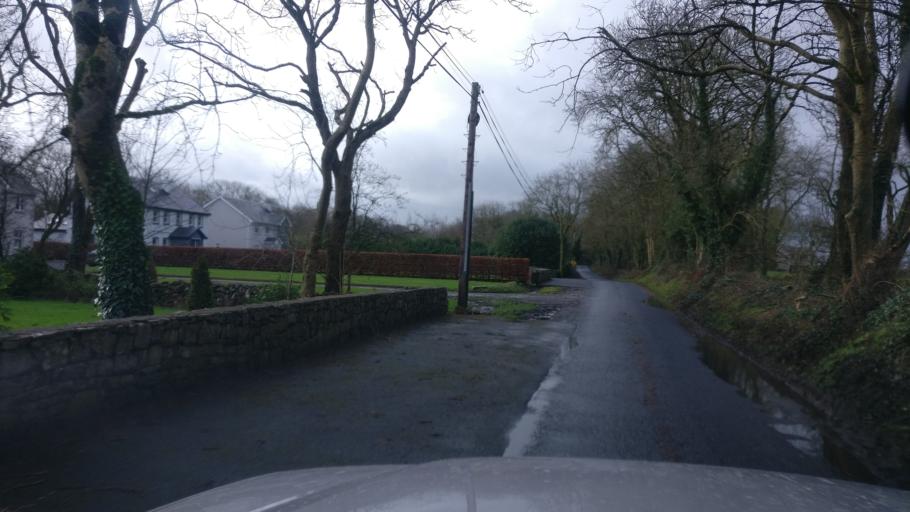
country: IE
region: Connaught
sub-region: County Galway
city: Athenry
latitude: 53.2728
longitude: -8.7700
